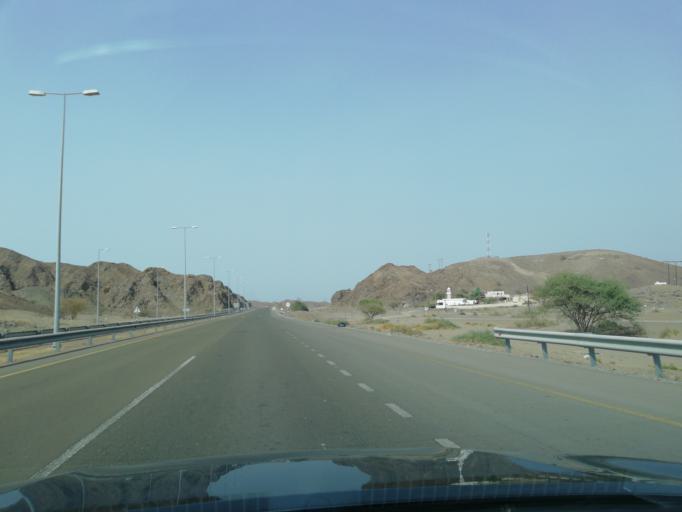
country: OM
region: Al Batinah
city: Al Liwa'
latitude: 24.3356
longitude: 56.4942
